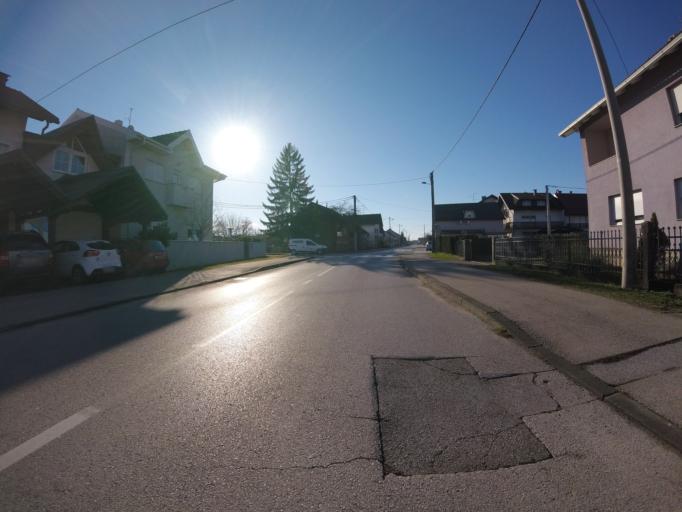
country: HR
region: Zagrebacka
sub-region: Grad Velika Gorica
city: Velika Gorica
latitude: 45.7031
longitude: 16.0747
